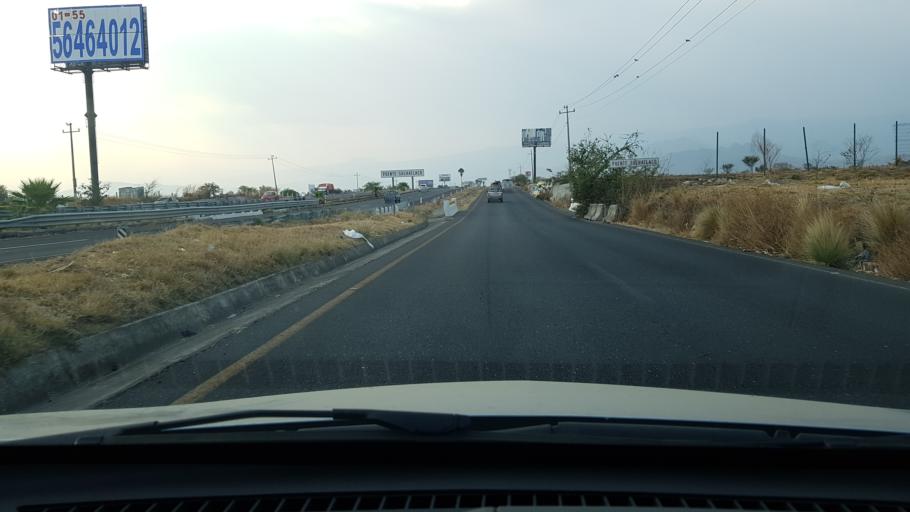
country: MX
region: Morelos
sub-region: Cuautla
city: Tierra Larga (Campo Nuevo)
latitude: 18.8683
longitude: -98.9524
